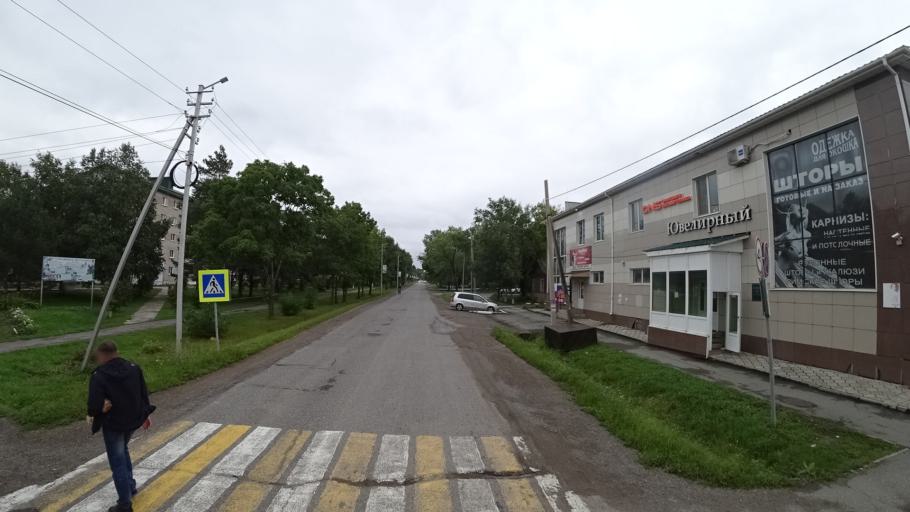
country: RU
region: Primorskiy
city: Chernigovka
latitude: 44.3430
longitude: 132.5755
